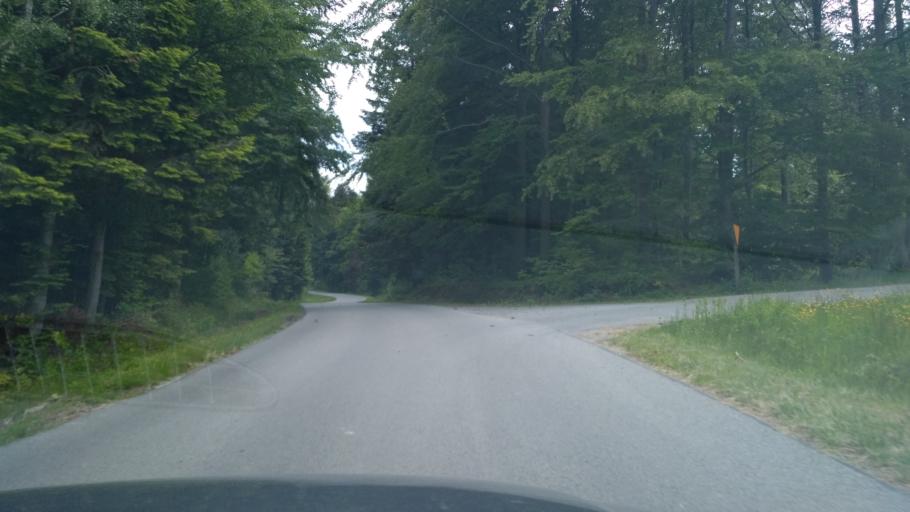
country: PL
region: Subcarpathian Voivodeship
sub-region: Powiat ropczycko-sedziszowski
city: Wielopole Skrzynskie
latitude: 49.9845
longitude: 21.6175
